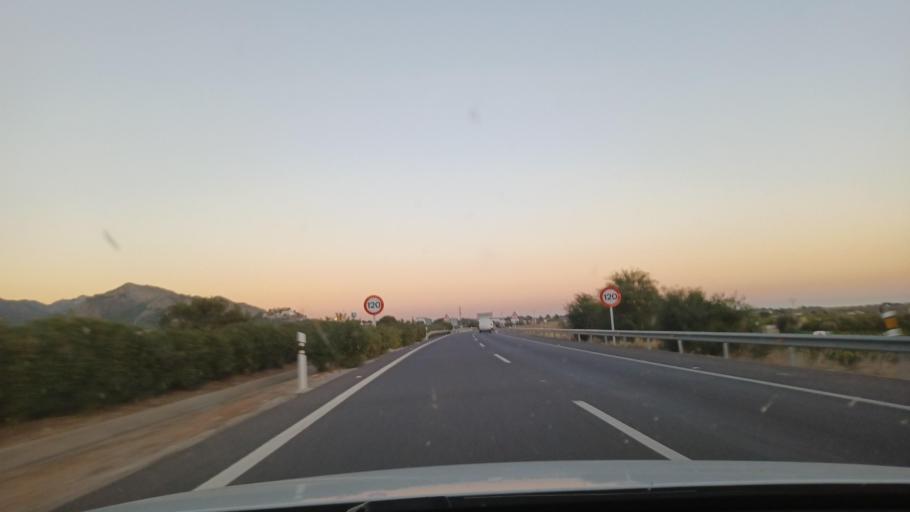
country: ES
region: Valencia
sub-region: Provincia de Castello
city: Castello de la Plana
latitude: 40.0284
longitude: -0.0239
